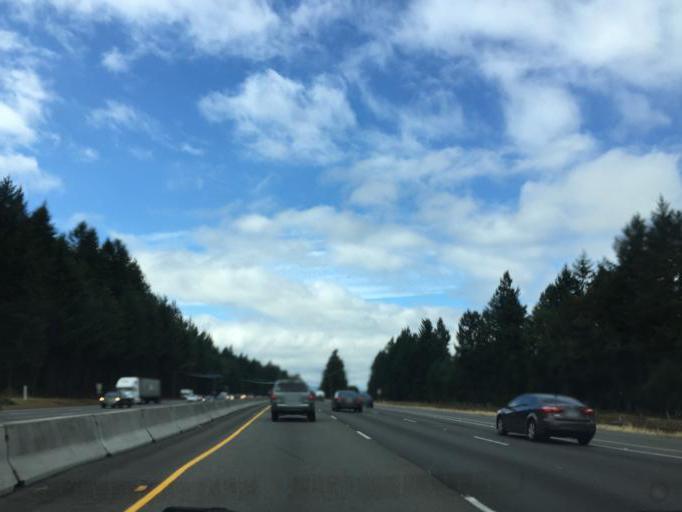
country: US
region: Washington
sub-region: Pierce County
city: DuPont
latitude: 47.0856
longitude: -122.6548
